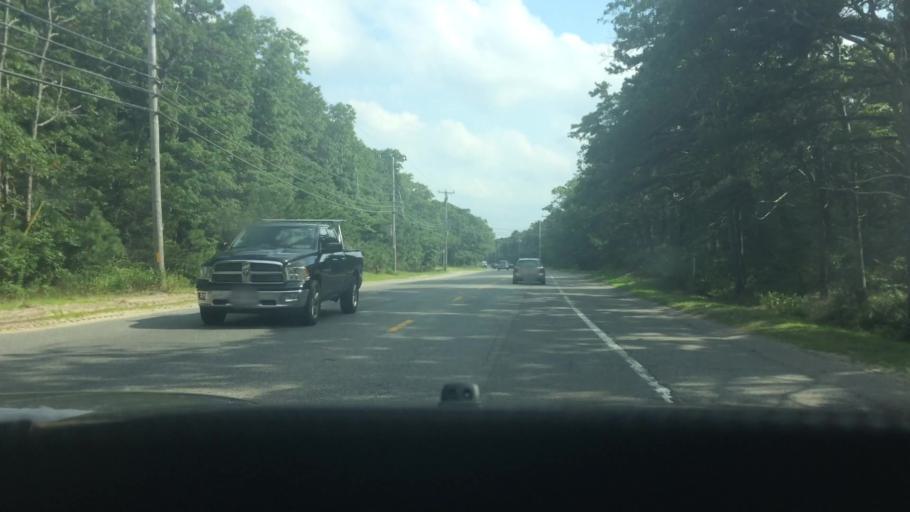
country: US
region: Massachusetts
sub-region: Barnstable County
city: Sandwich
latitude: 41.7291
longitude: -70.4902
